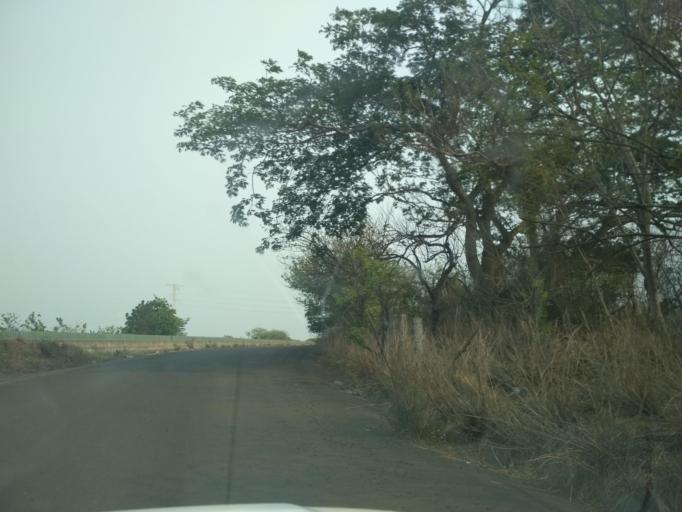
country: MX
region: Veracruz
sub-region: Veracruz
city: Las Amapolas
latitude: 19.1376
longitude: -96.2538
